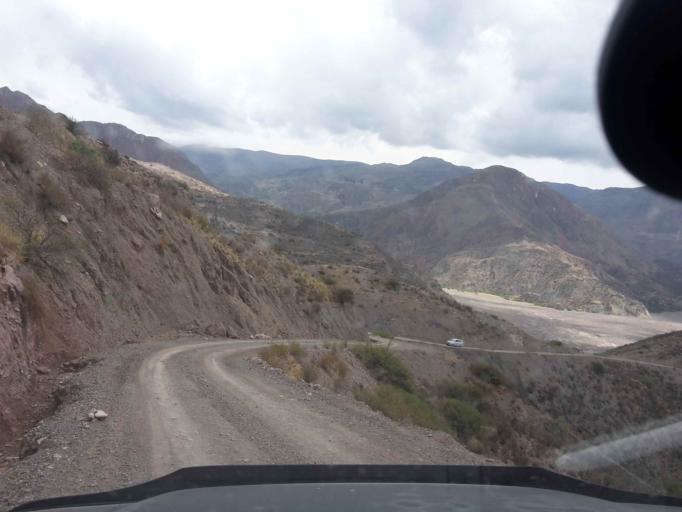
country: BO
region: Cochabamba
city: Colchani
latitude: -17.5150
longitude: -66.6078
